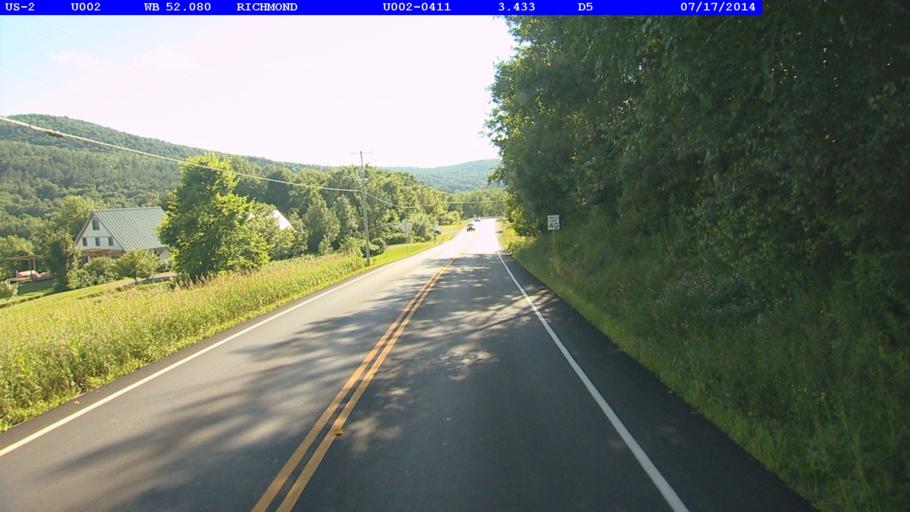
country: US
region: Vermont
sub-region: Chittenden County
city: Williston
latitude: 44.4015
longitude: -72.9808
